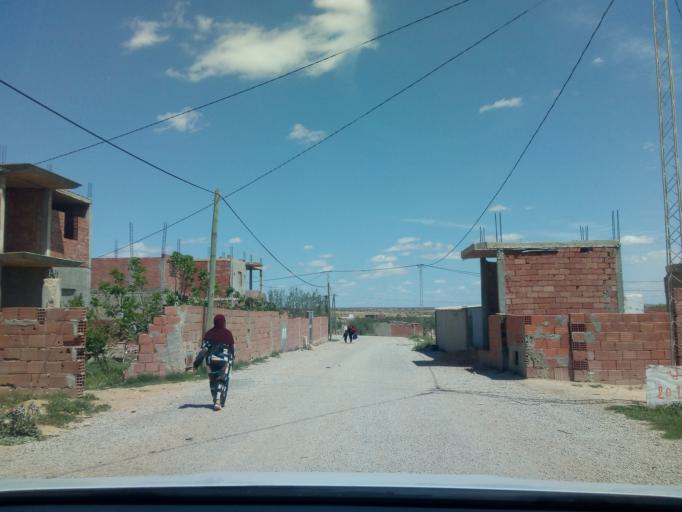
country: TN
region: Safaqis
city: Sfax
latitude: 34.7306
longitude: 10.4920
